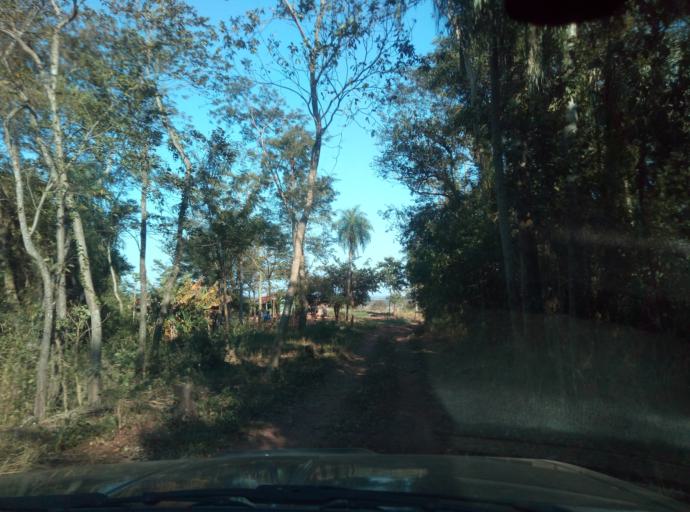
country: PY
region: Caaguazu
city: San Joaquin
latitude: -25.1685
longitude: -56.1143
